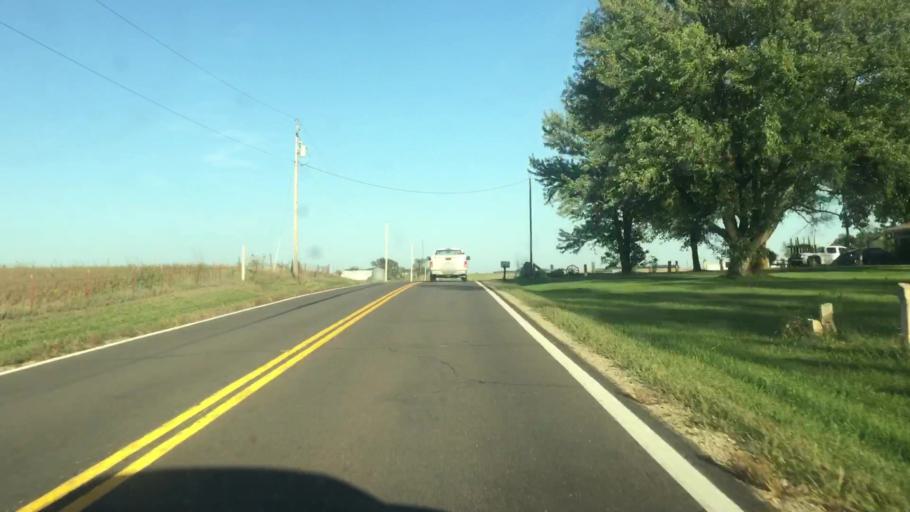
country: US
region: Kansas
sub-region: Brown County
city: Horton
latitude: 39.5516
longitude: -95.4500
